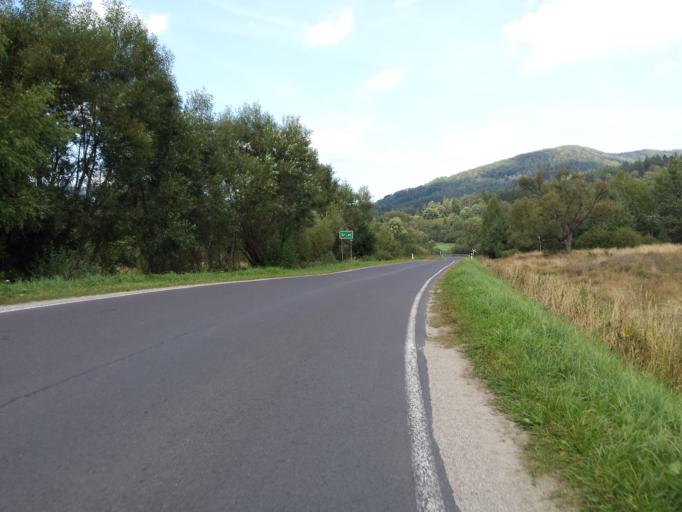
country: PL
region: Subcarpathian Voivodeship
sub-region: Powiat leski
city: Cisna
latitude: 49.1790
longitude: 22.4346
